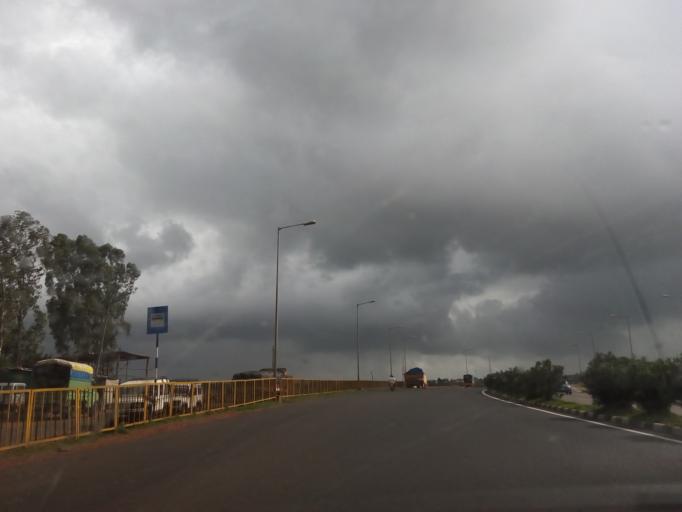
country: IN
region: Karnataka
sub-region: Belgaum
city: Belgaum
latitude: 16.0298
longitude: 74.5305
